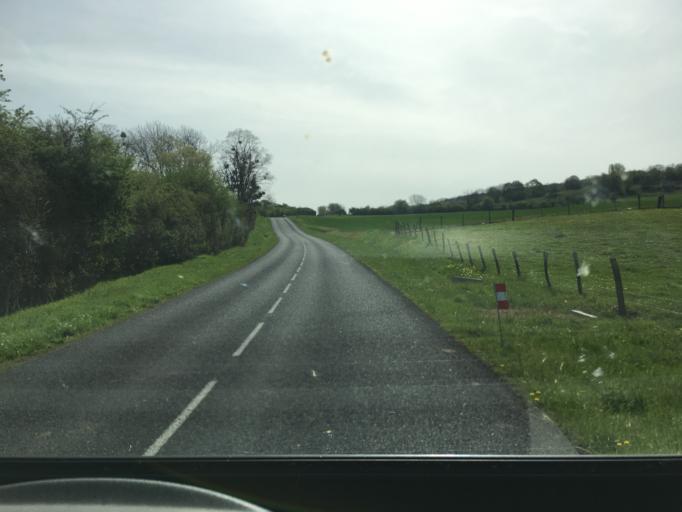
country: FR
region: Lorraine
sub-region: Departement de Meurthe-et-Moselle
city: Dommartin-les-Toul
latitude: 48.6713
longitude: 5.9315
